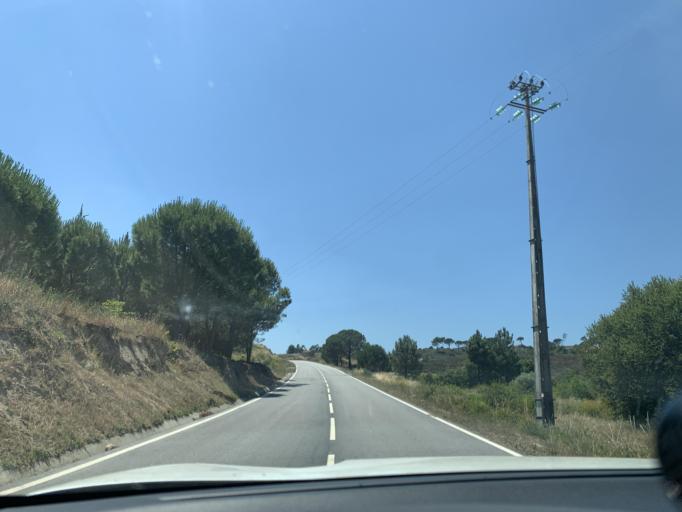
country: PT
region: Viseu
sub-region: Mangualde
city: Mangualde
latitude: 40.5664
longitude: -7.6754
